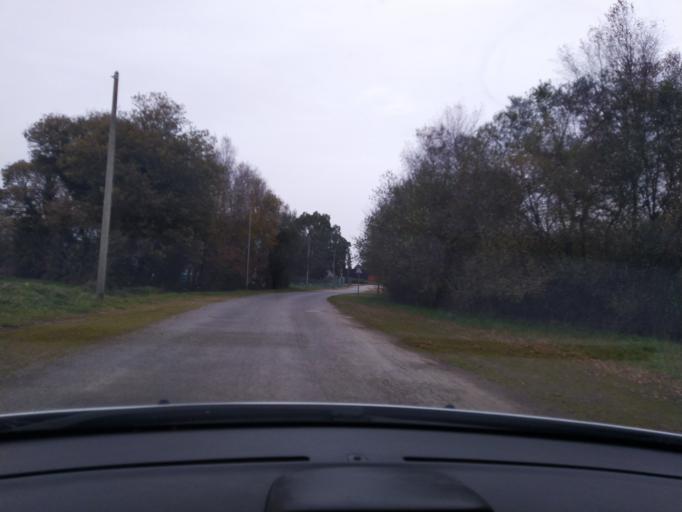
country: FR
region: Brittany
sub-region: Departement du Finistere
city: Guerlesquin
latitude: 48.5107
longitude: -3.5847
